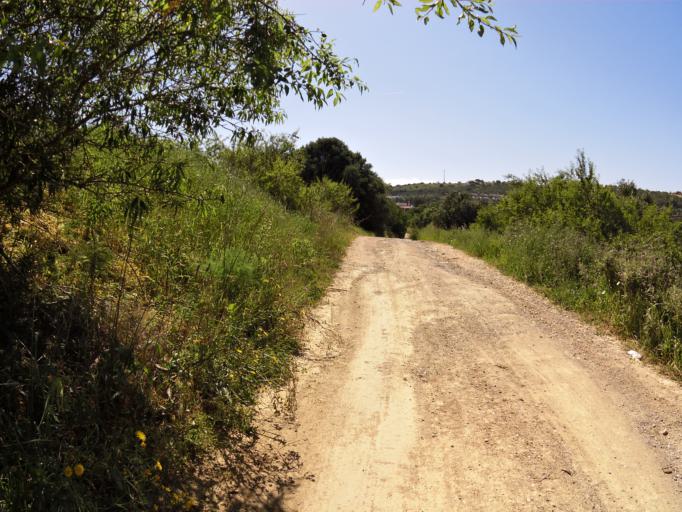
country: PT
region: Faro
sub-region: Lagos
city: Lagos
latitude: 37.1009
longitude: -8.7121
